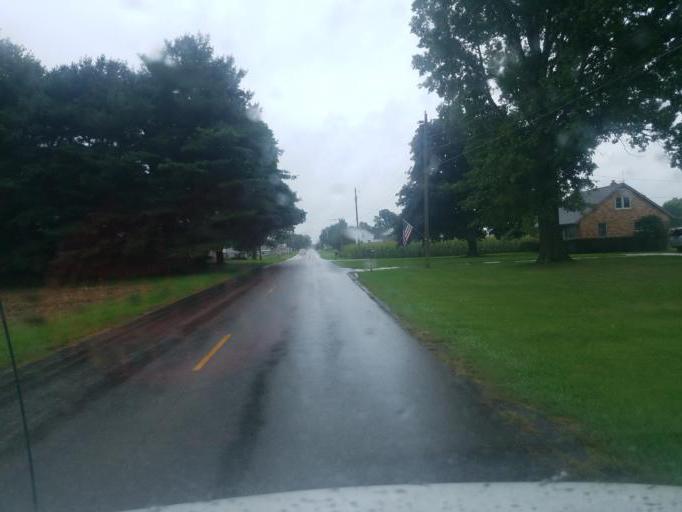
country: US
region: Ohio
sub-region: Medina County
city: Seville
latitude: 40.9859
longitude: -81.8577
